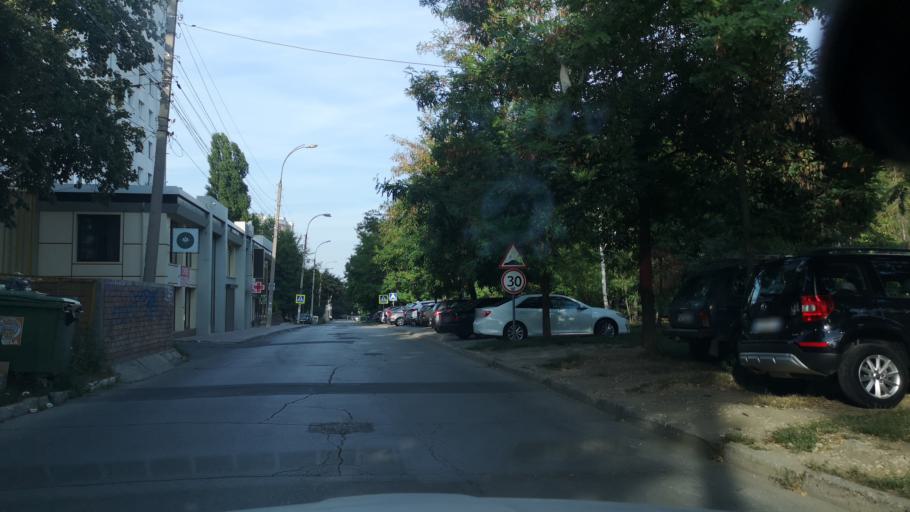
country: MD
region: Chisinau
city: Chisinau
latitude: 47.0054
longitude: 28.8469
